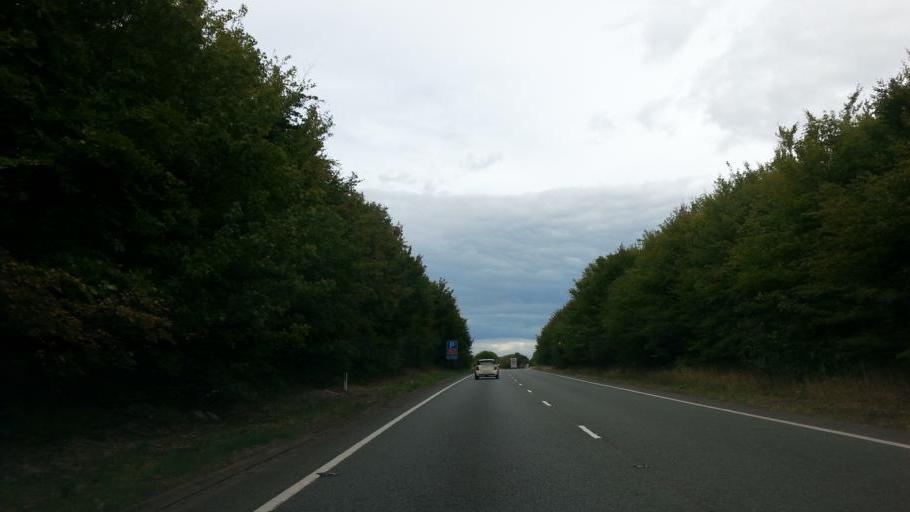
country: GB
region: England
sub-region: Cambridgeshire
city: Duxford
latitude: 52.0858
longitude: 0.1988
